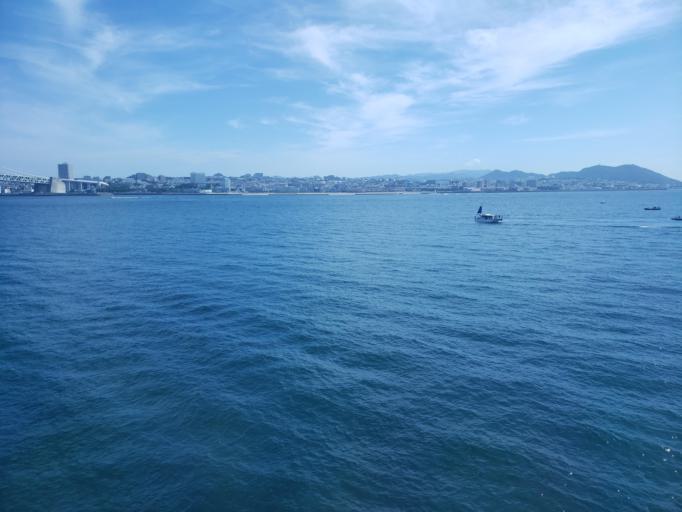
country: JP
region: Hyogo
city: Akashi
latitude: 34.6141
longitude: 135.0310
